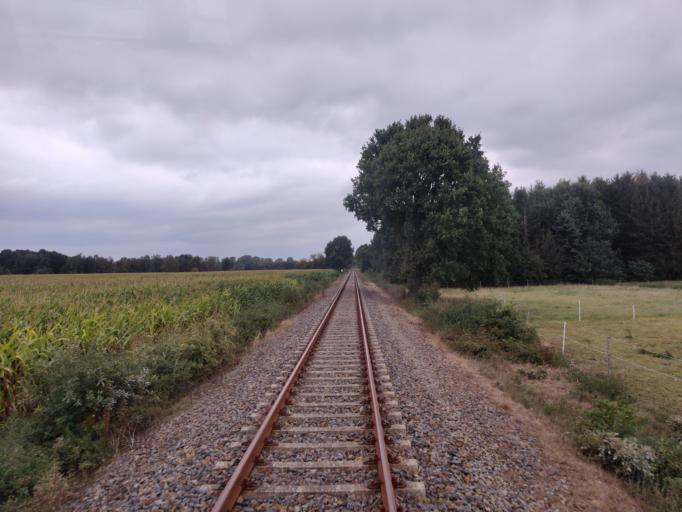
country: DE
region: Lower Saxony
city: Gnarrenburg
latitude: 53.3598
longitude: 9.0080
